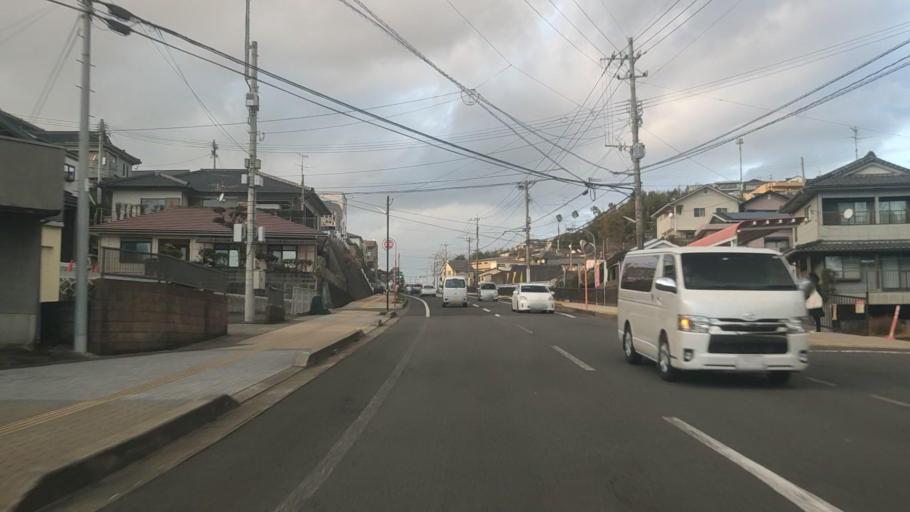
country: JP
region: Kagoshima
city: Kagoshima-shi
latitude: 31.6163
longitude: 130.5549
